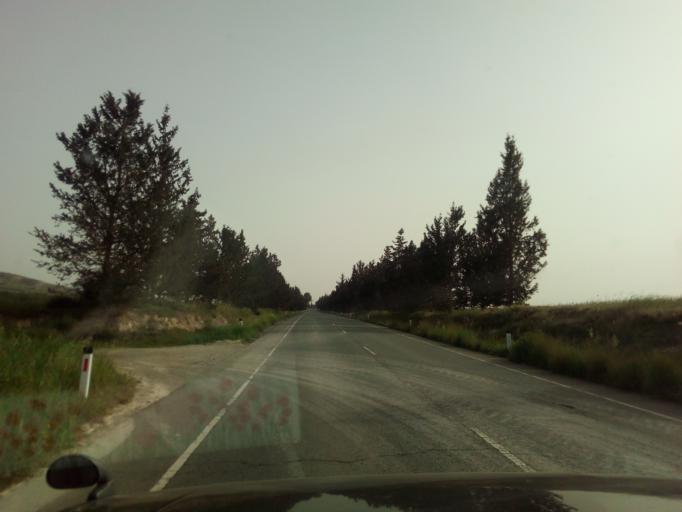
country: CY
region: Lefkosia
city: Lympia
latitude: 35.0197
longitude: 33.4950
